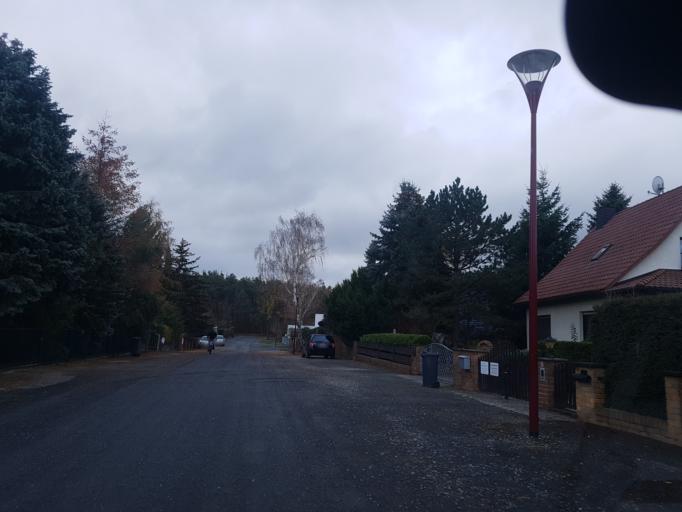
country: DE
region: Brandenburg
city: Finsterwalde
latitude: 51.6405
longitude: 13.6813
